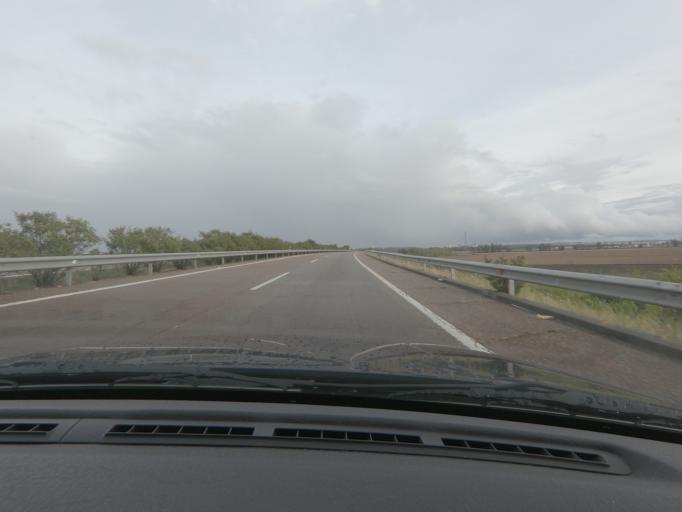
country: ES
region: Extremadura
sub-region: Provincia de Badajoz
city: Badajoz
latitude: 38.9175
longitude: -6.9533
